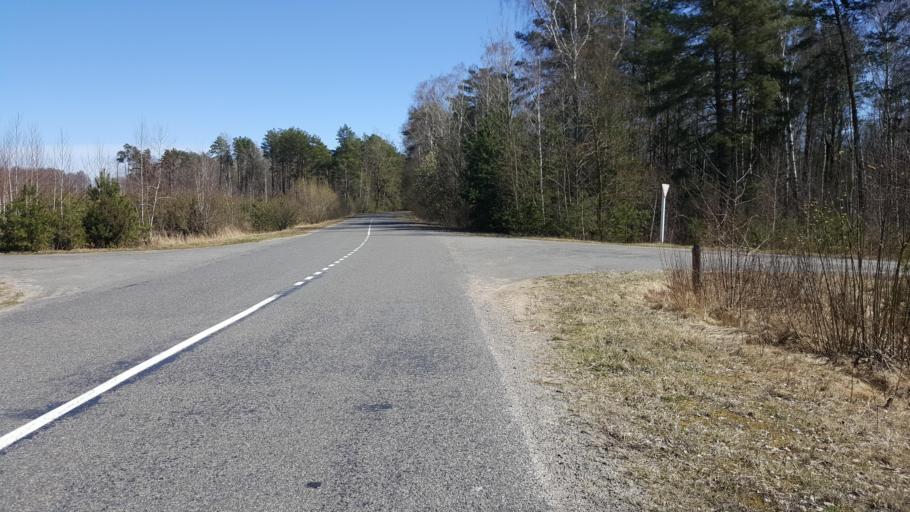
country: BY
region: Brest
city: Zhabinka
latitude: 52.2399
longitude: 23.9539
